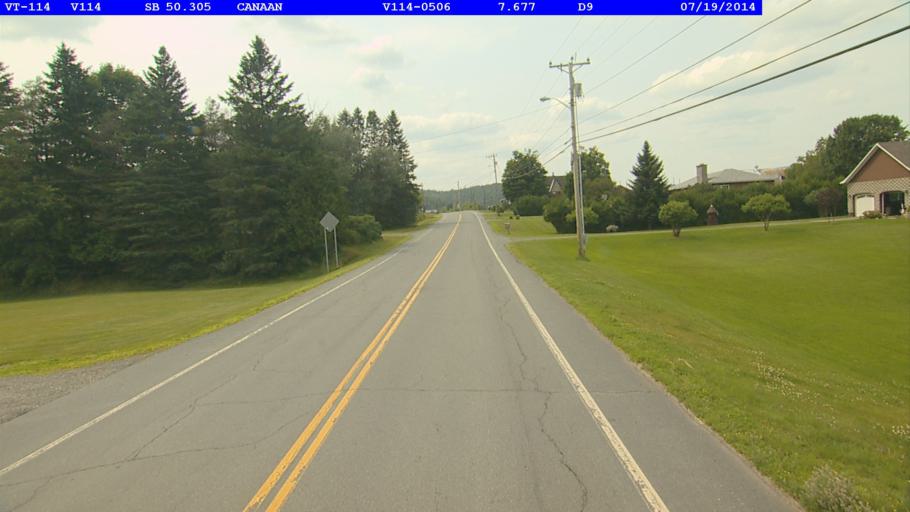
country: US
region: New Hampshire
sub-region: Coos County
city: Colebrook
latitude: 45.0009
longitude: -71.5462
